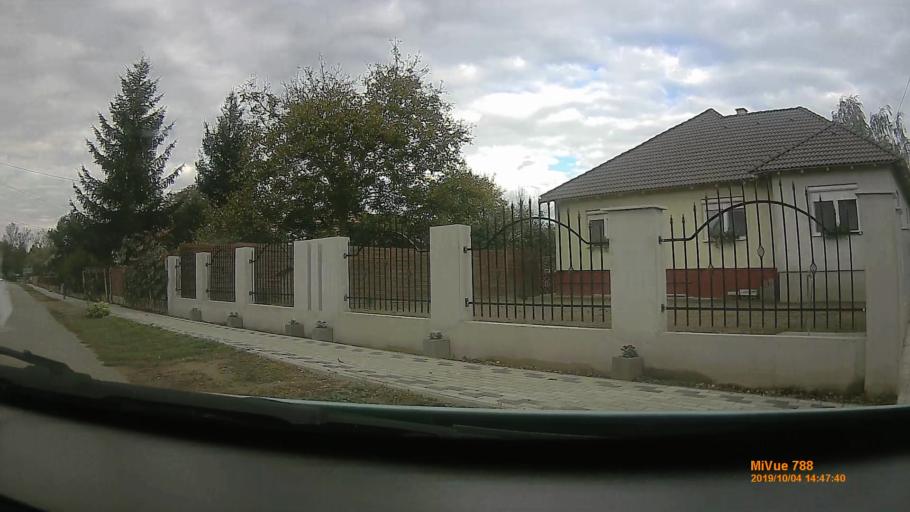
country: HU
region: Szabolcs-Szatmar-Bereg
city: Nyirpazony
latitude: 47.9894
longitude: 21.8010
